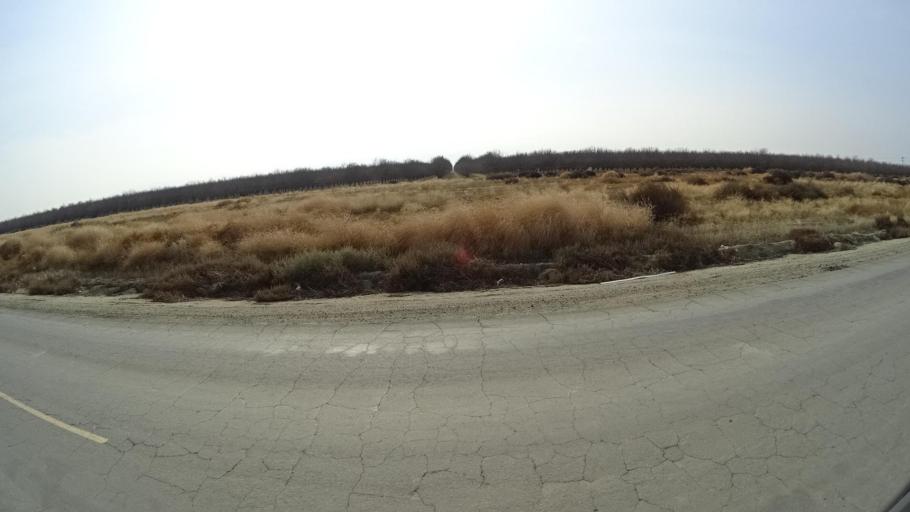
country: US
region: California
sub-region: Kern County
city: Greenfield
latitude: 35.0947
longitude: -119.0978
